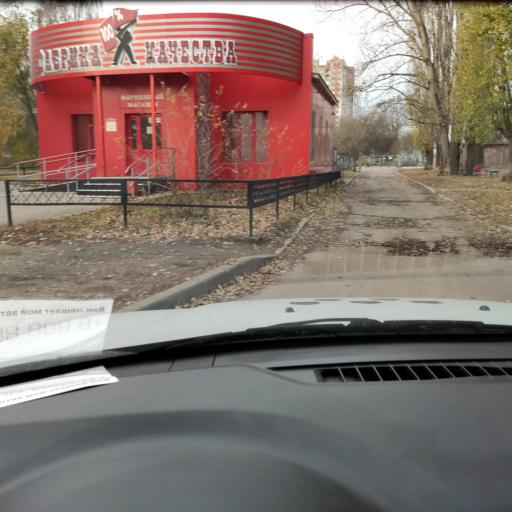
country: RU
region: Samara
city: Tol'yatti
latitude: 53.5085
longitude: 49.4368
